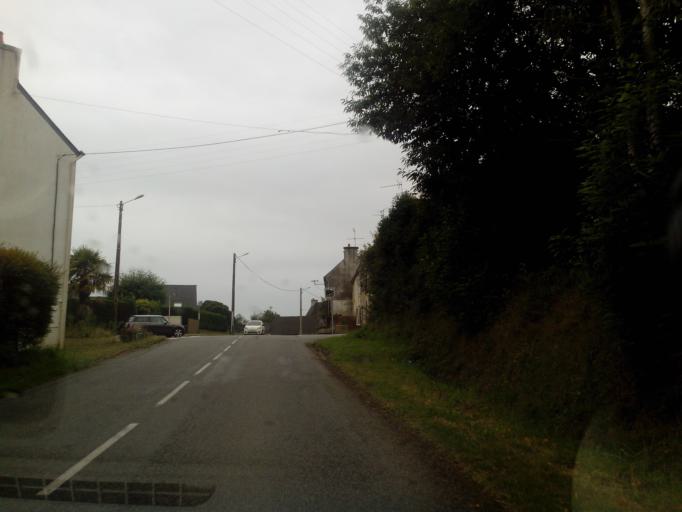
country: FR
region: Brittany
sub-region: Departement du Finistere
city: Tremeven
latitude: 47.9070
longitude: -3.5193
